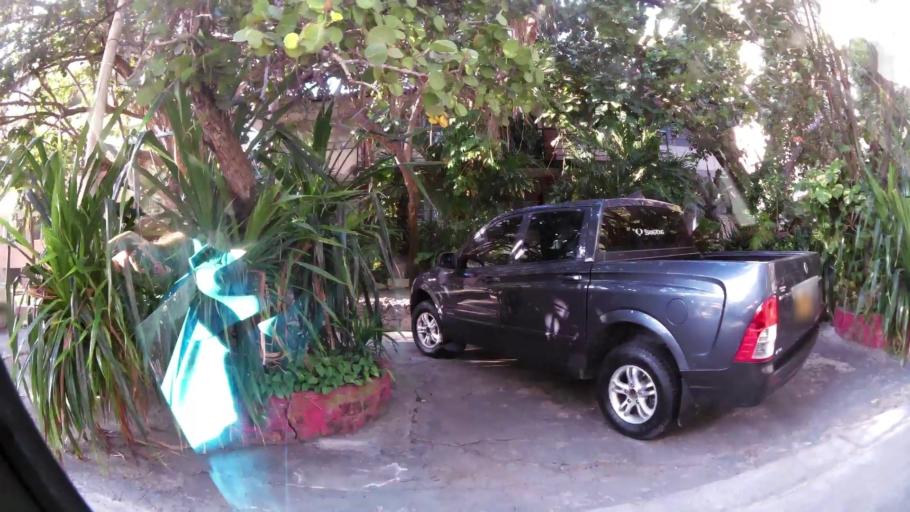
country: CO
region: Atlantico
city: Barranquilla
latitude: 11.0056
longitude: -74.8147
